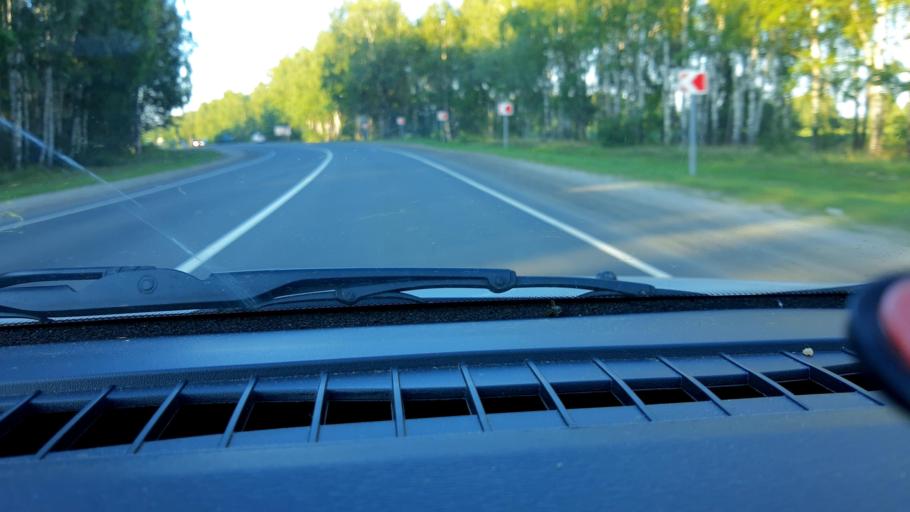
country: RU
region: Nizjnij Novgorod
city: Linda
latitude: 56.6099
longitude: 44.0553
